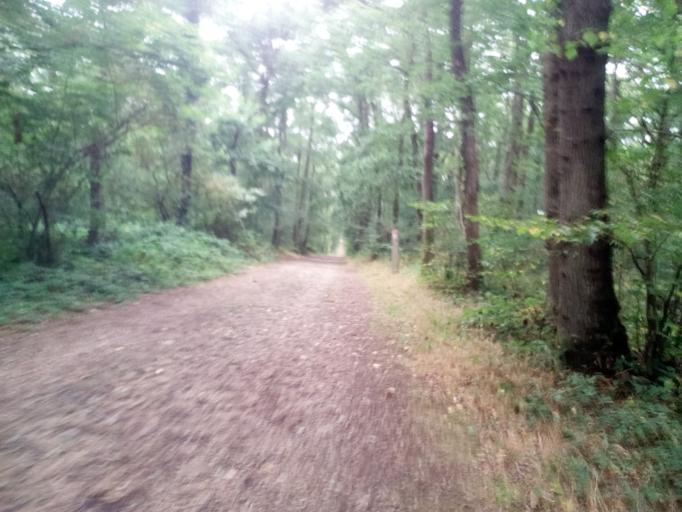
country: FR
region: Lower Normandy
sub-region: Departement du Calvados
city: Clinchamps-sur-Orne
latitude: 49.0453
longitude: -0.4311
